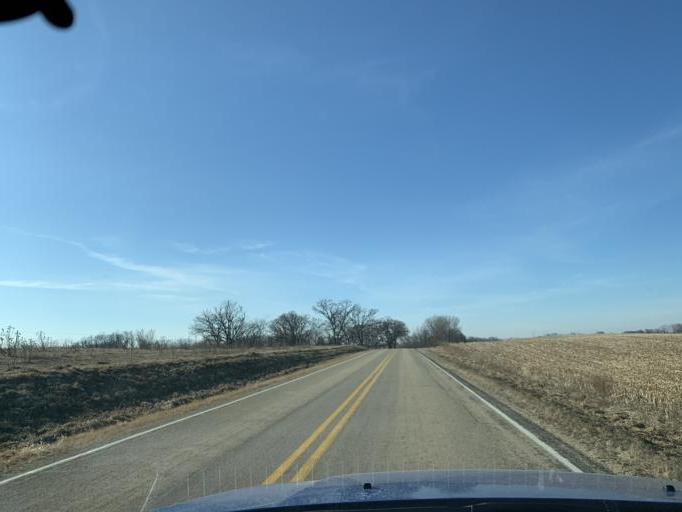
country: US
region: Wisconsin
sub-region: Iowa County
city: Barneveld
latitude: 42.8148
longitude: -89.9102
